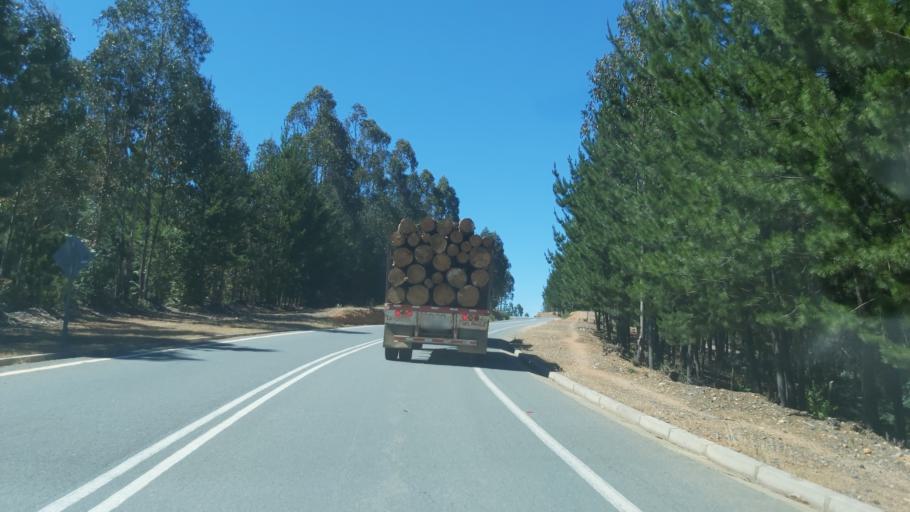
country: CL
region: Maule
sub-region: Provincia de Talca
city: Constitucion
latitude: -34.9314
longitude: -71.9868
